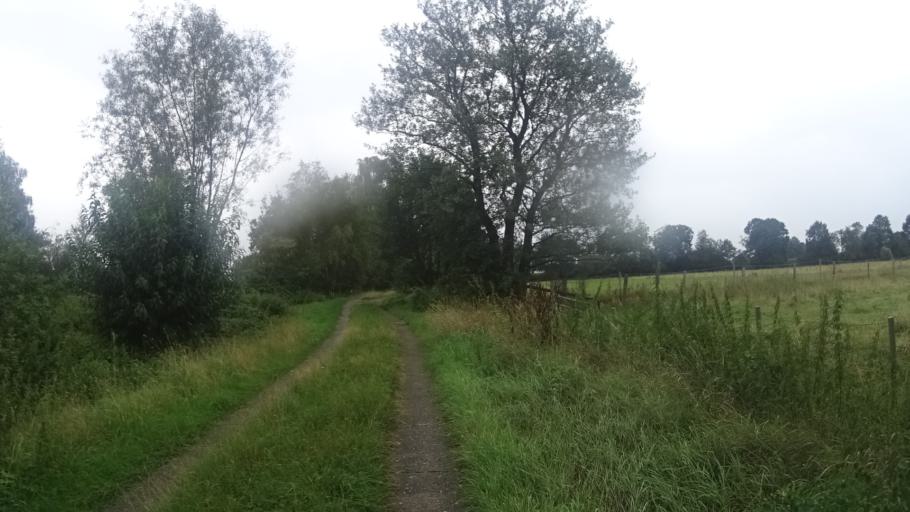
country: DE
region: Schleswig-Holstein
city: Heede
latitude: 53.7596
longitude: 9.8046
